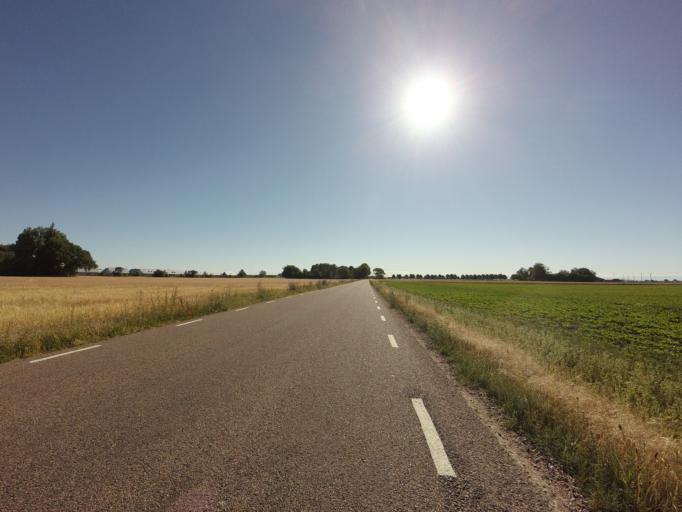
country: SE
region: Skane
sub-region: Vellinge Kommun
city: Hollviken
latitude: 55.4042
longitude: 13.0010
